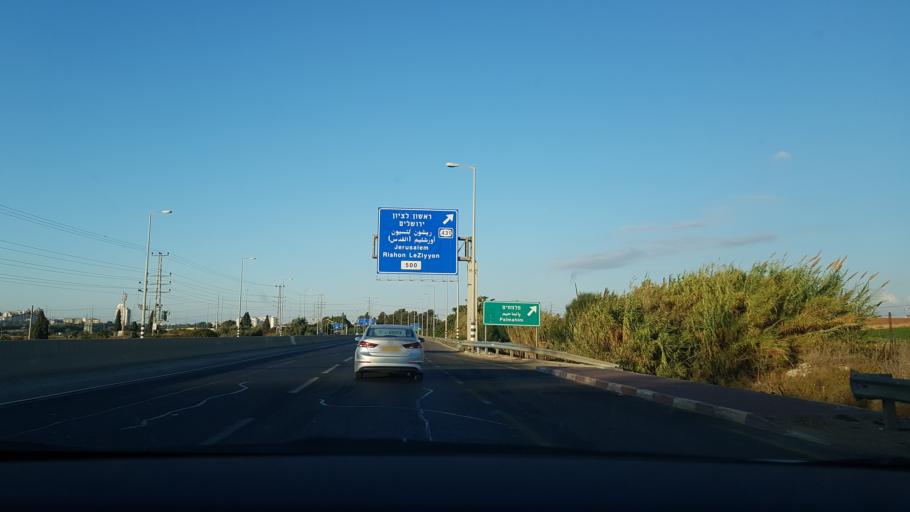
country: IL
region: Central District
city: Ness Ziona
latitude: 31.9440
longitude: 34.7812
